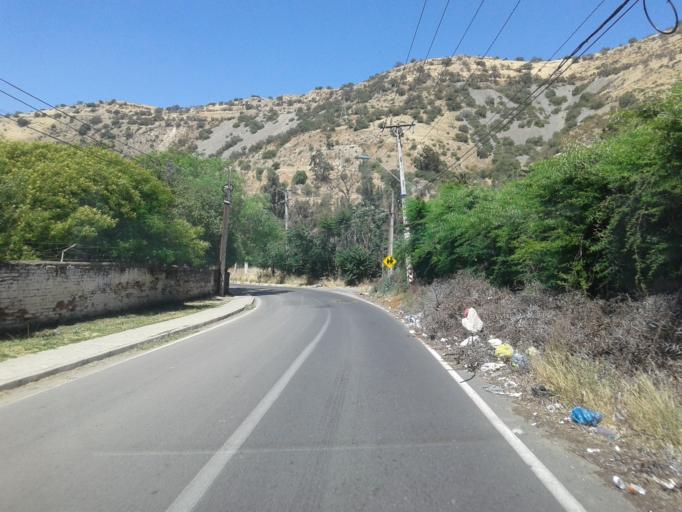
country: CL
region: Valparaiso
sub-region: Provincia de Quillota
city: Hacienda La Calera
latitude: -32.7992
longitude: -71.1965
